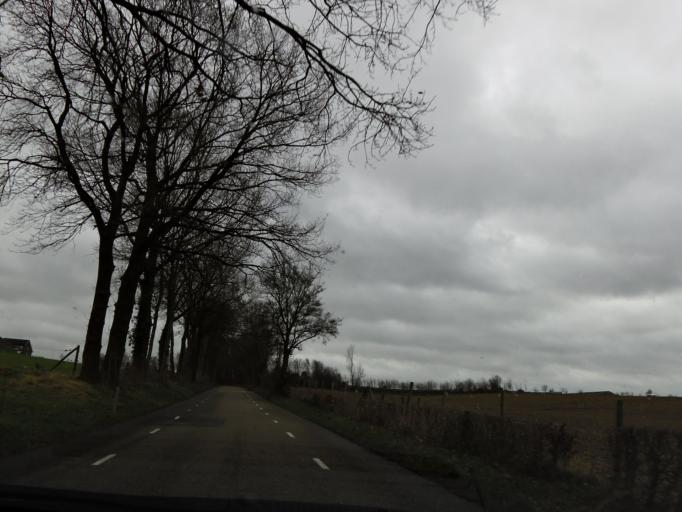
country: NL
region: Limburg
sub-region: Eijsden-Margraten
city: Margraten
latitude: 50.7980
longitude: 5.8043
